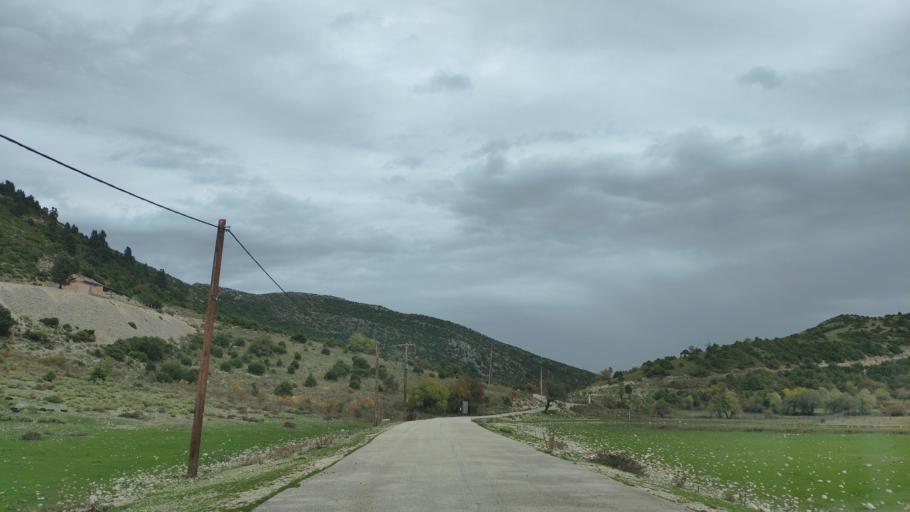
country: GR
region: Epirus
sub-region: Nomos Thesprotias
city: Paramythia
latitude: 39.4481
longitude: 20.6456
